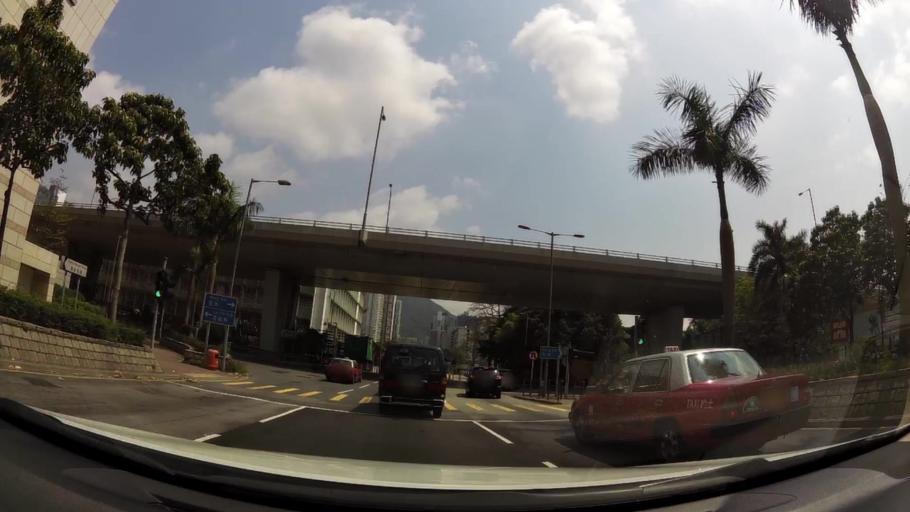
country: HK
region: Sham Shui Po
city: Sham Shui Po
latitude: 22.3307
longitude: 114.1540
